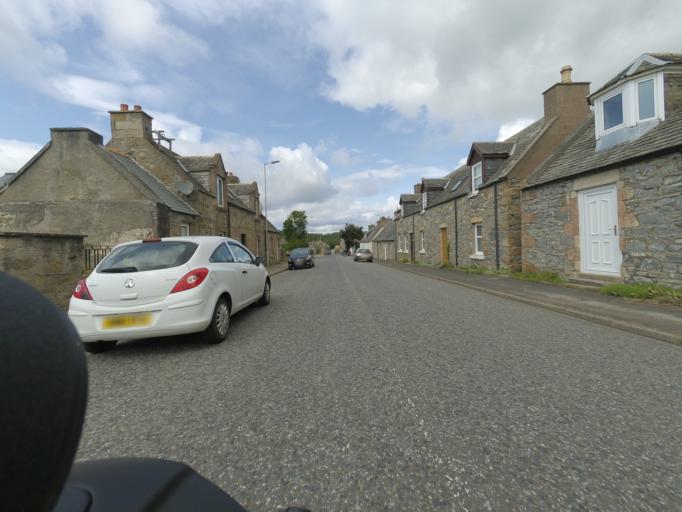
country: GB
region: Scotland
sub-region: Highland
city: Grantown on Spey
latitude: 57.2529
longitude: -3.3809
